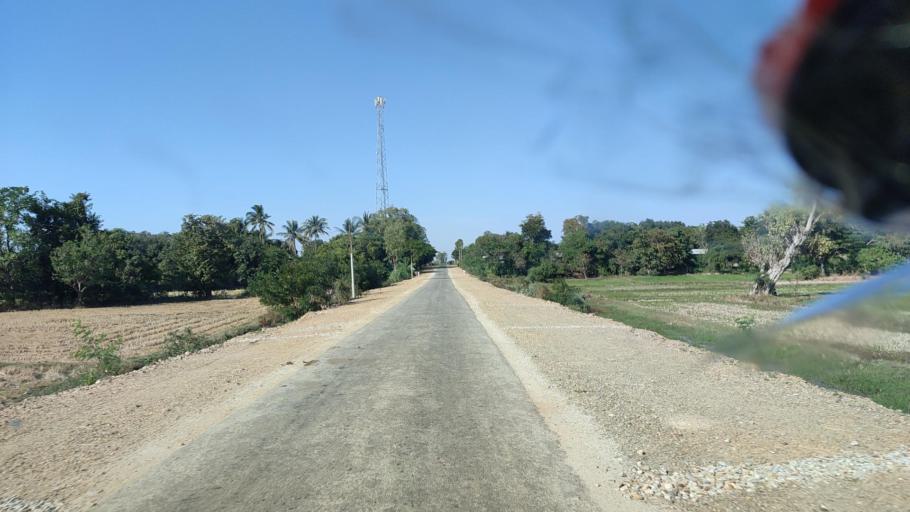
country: MM
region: Mandalay
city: Pyinmana
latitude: 20.0838
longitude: 96.2650
